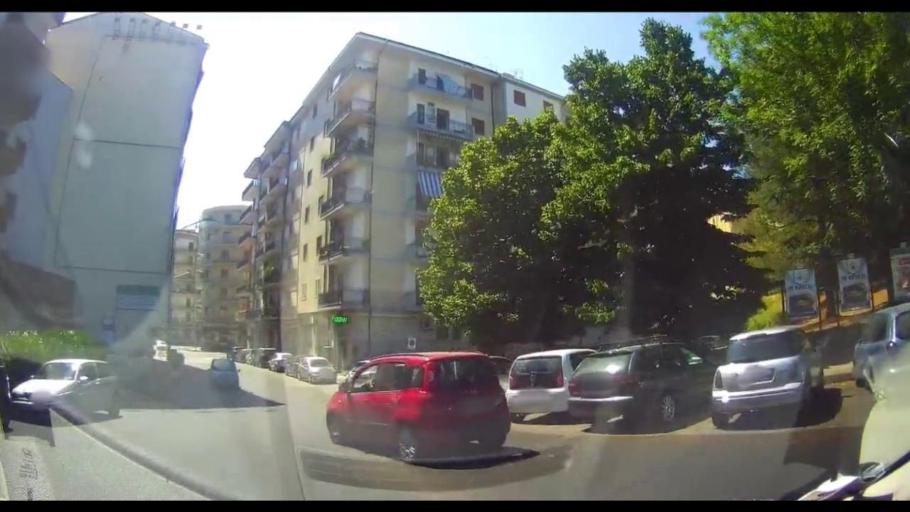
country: IT
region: Calabria
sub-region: Provincia di Cosenza
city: Cosenza
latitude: 39.3093
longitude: 16.2511
